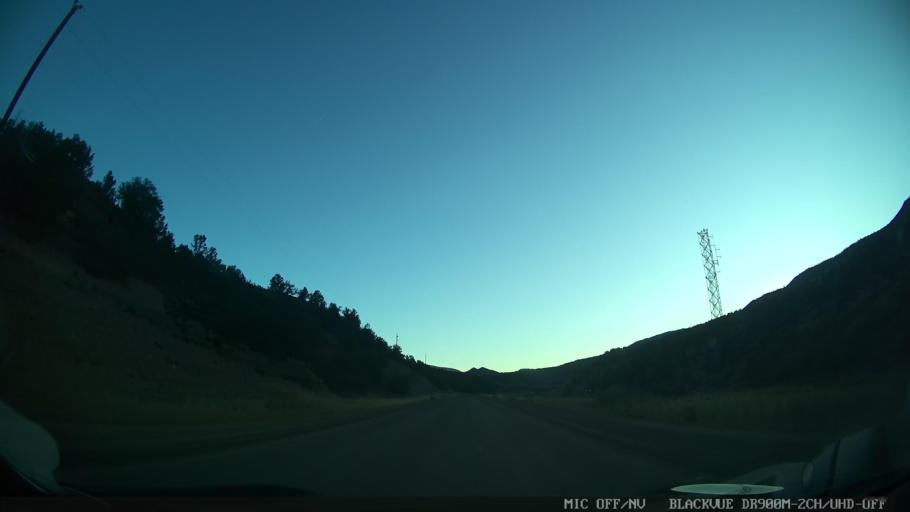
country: US
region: Colorado
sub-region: Eagle County
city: Edwards
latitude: 39.8875
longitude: -106.6228
